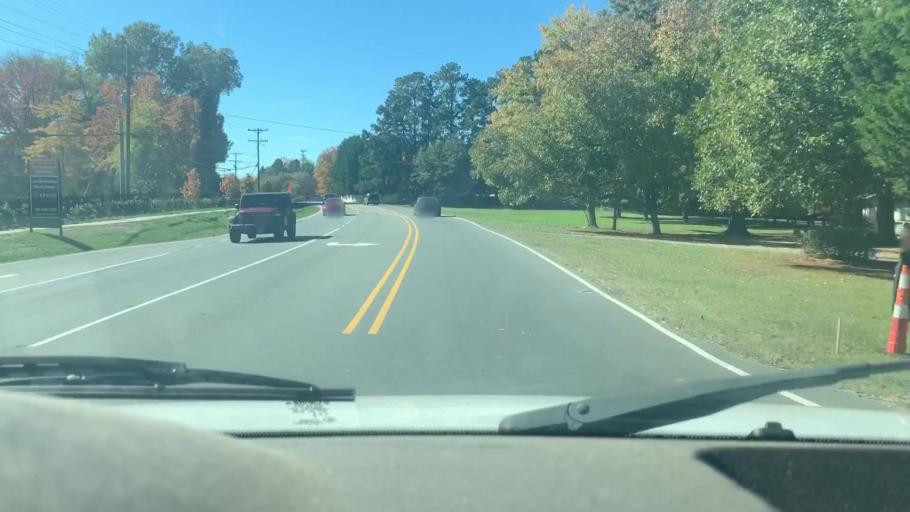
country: US
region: North Carolina
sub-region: Mecklenburg County
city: Huntersville
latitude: 35.4309
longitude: -80.9102
